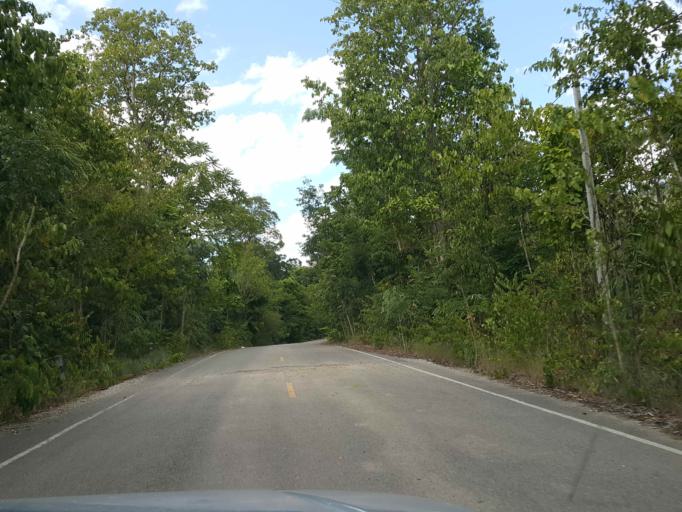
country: TH
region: Lampang
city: Thoen
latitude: 17.6460
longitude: 99.2901
